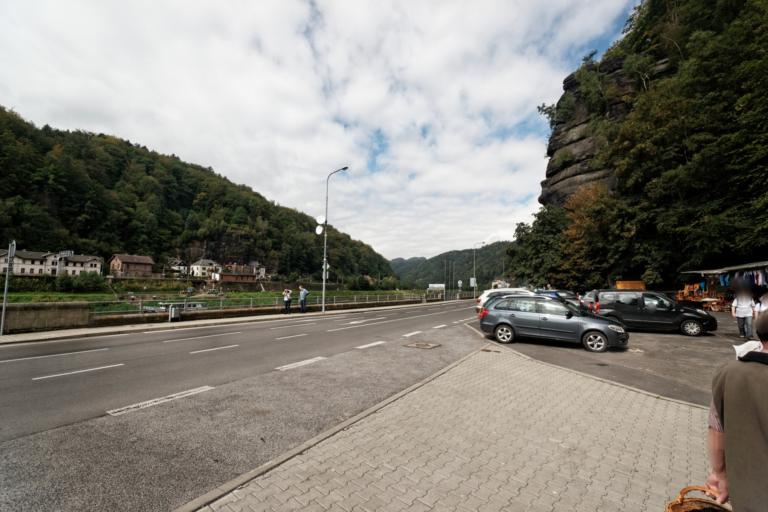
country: DE
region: Saxony
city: Bad Schandau
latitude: 50.8742
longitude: 14.2364
